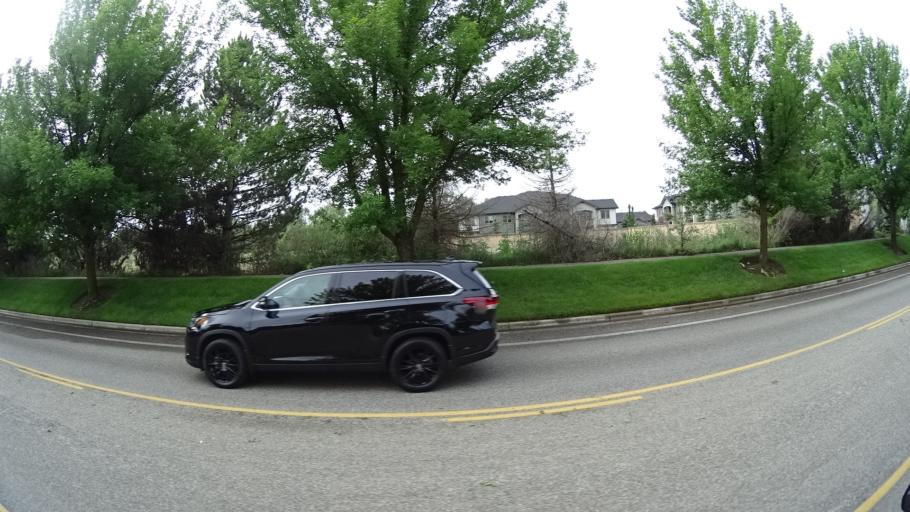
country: US
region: Idaho
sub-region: Ada County
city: Eagle
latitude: 43.6886
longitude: -116.3425
